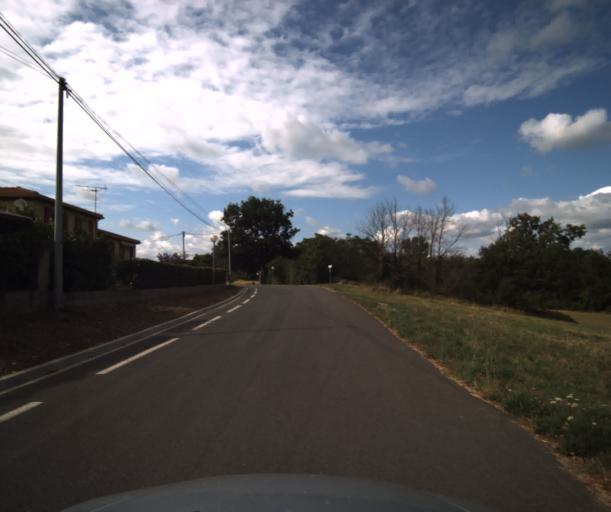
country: FR
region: Midi-Pyrenees
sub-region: Departement de la Haute-Garonne
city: Muret
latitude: 43.4457
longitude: 1.3250
